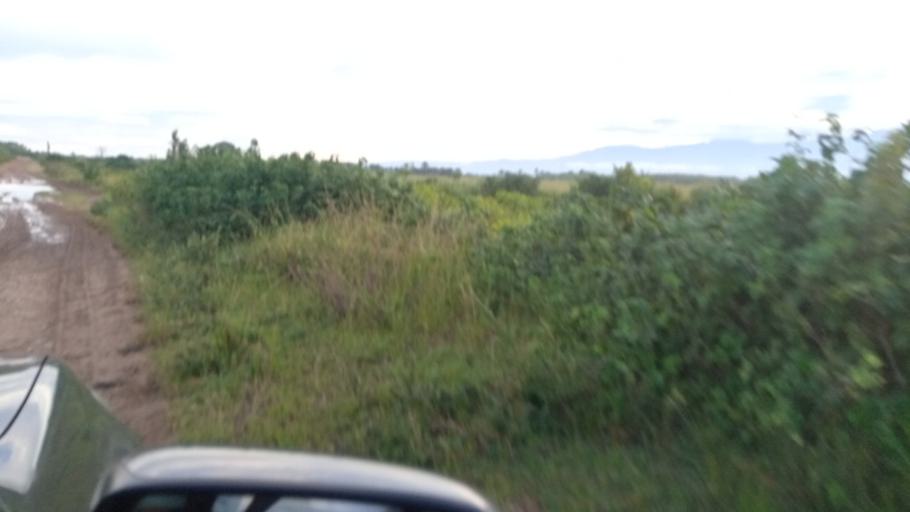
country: BI
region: Bujumbura Mairie
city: Bujumbura
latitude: -3.4673
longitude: 29.3422
